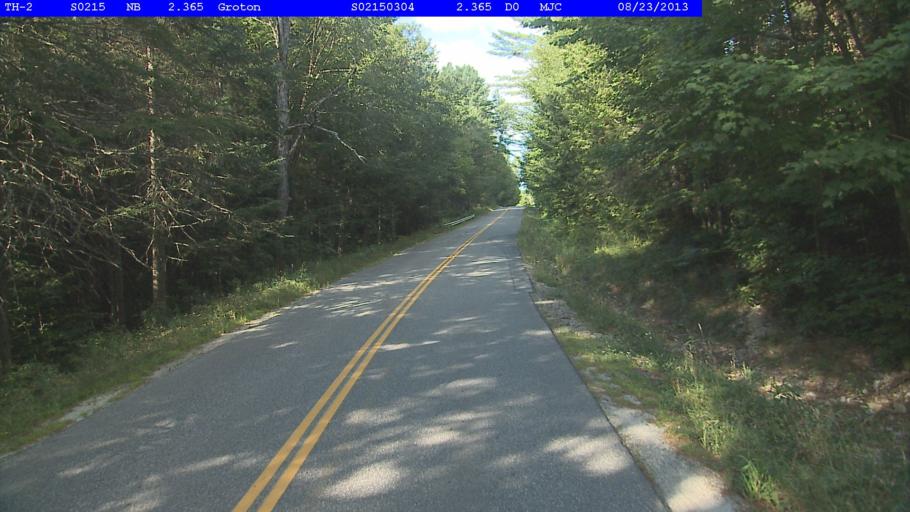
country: US
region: New Hampshire
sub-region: Grafton County
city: Woodsville
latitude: 44.2414
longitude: -72.1821
